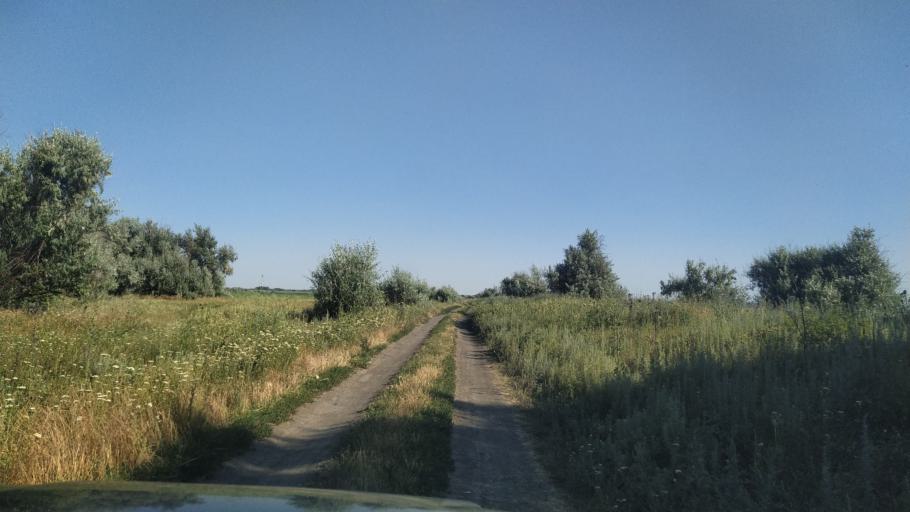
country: RU
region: Rostov
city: Kuleshovka
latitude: 47.1333
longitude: 39.6422
